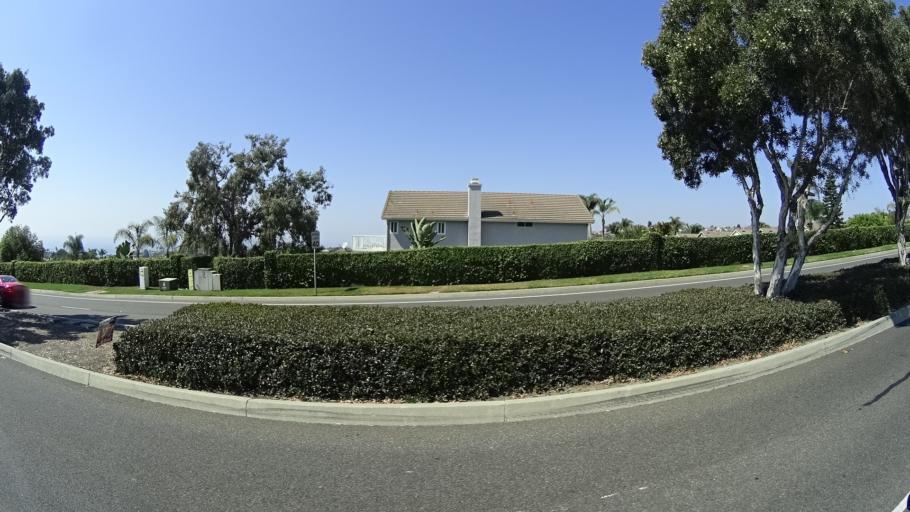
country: US
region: California
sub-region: Orange County
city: San Clemente
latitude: 33.4487
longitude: -117.6272
